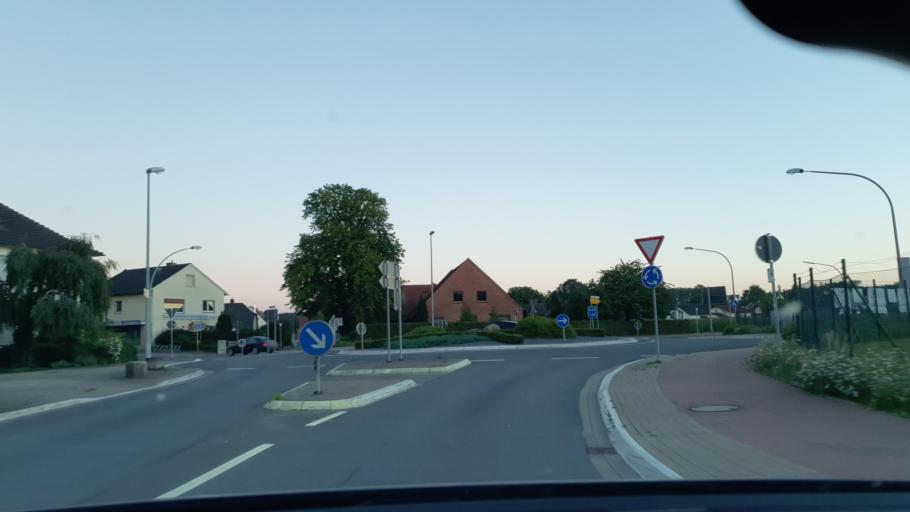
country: DE
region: North Rhine-Westphalia
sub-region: Regierungsbezirk Detmold
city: Rodinghausen
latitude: 52.1982
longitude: 8.4549
